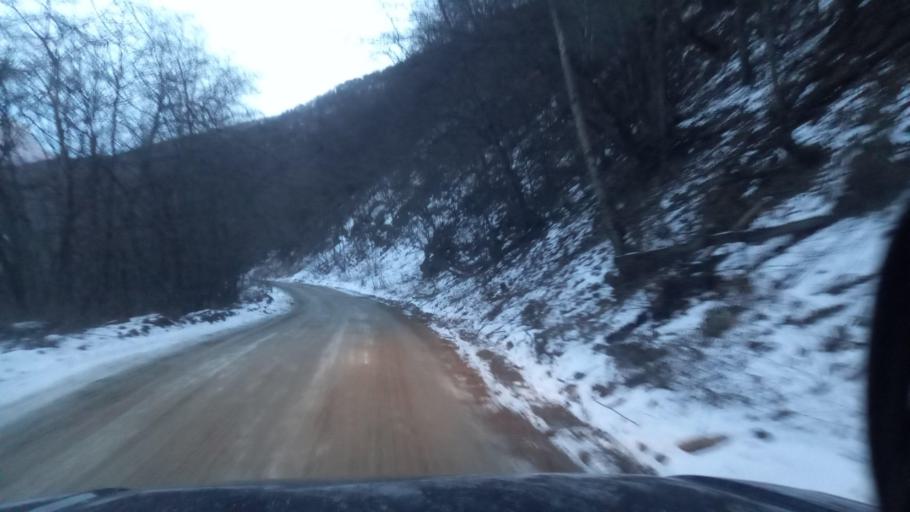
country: RU
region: Ingushetiya
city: Dzhayrakh
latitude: 42.8253
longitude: 44.5909
